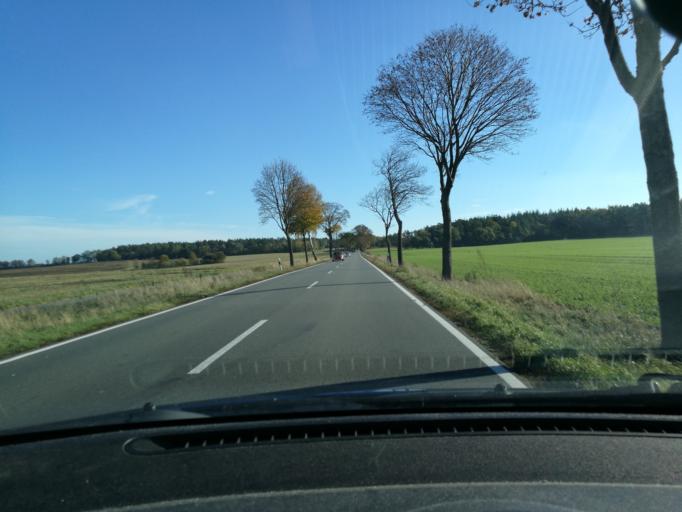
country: DE
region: Lower Saxony
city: Nahrendorf
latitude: 53.1566
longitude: 10.8162
